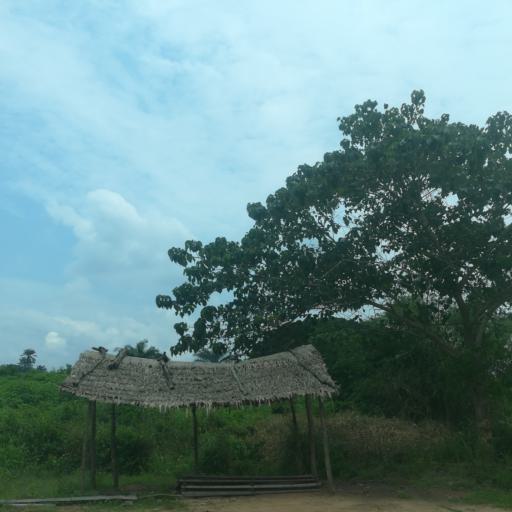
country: NG
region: Lagos
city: Ejirin
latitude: 6.6594
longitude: 3.8174
